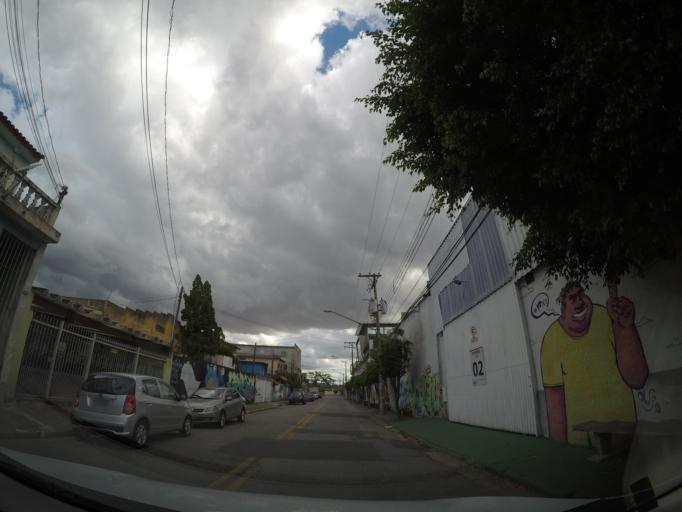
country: BR
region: Sao Paulo
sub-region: Guarulhos
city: Guarulhos
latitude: -23.4813
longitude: -46.5536
